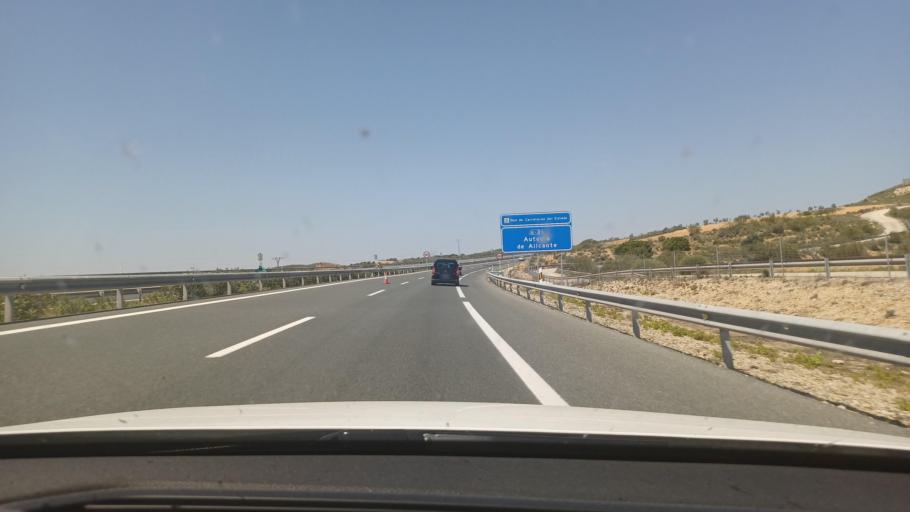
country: ES
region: Castille-La Mancha
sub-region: Provincia de Albacete
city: Almansa
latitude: 38.8758
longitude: -1.1776
